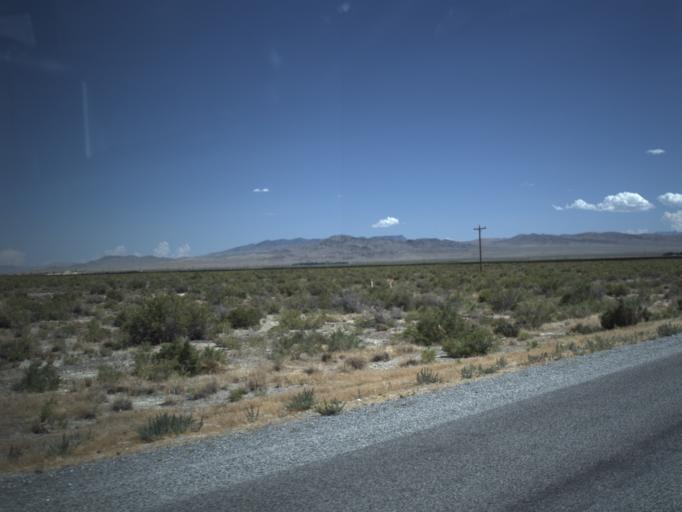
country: US
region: Nevada
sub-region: White Pine County
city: McGill
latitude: 39.0571
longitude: -114.0483
